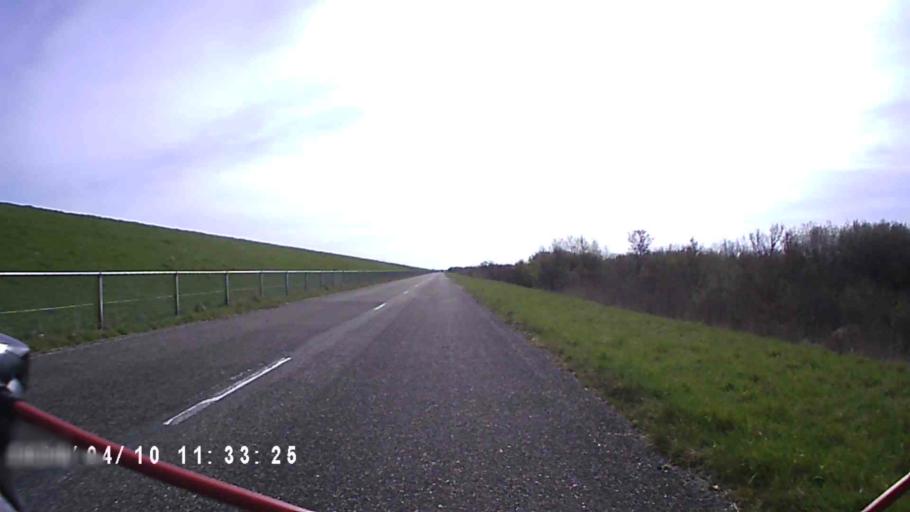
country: NL
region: Groningen
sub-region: Gemeente De Marne
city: Ulrum
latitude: 53.4087
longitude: 6.2742
